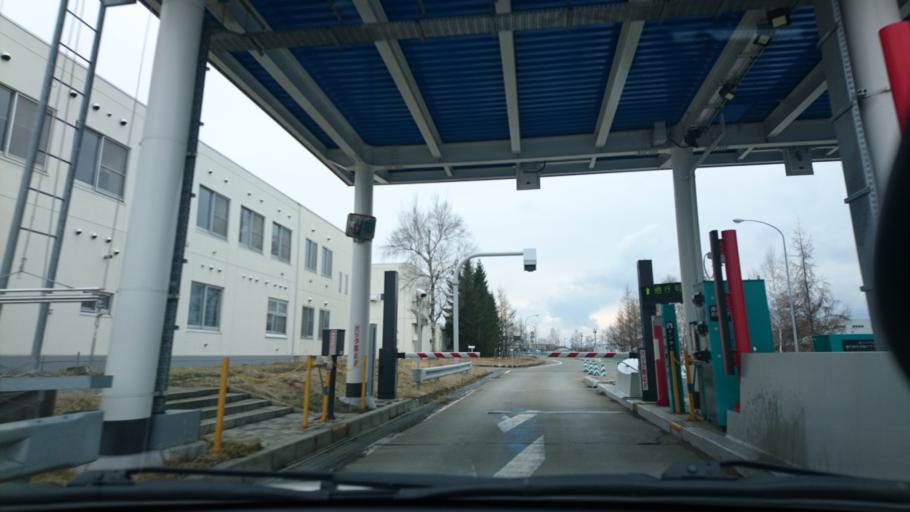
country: JP
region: Hokkaido
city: Otofuke
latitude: 42.9821
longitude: 143.1819
